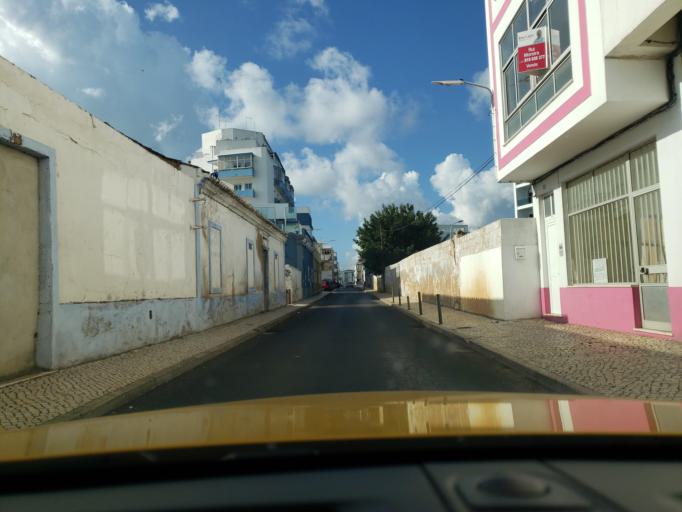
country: PT
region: Faro
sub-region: Portimao
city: Portimao
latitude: 37.1405
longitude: -8.5331
